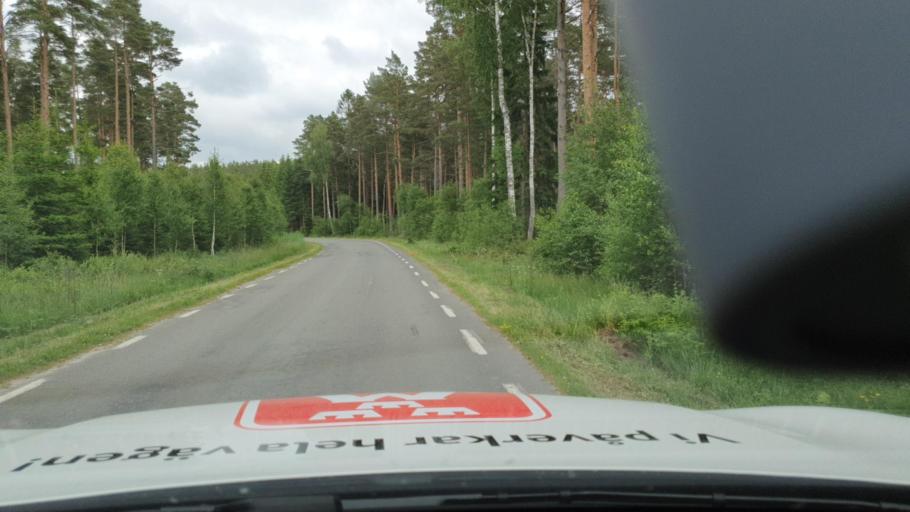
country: SE
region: Vaestra Goetaland
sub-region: Tidaholms Kommun
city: Olofstorp
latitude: 58.1904
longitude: 14.0880
